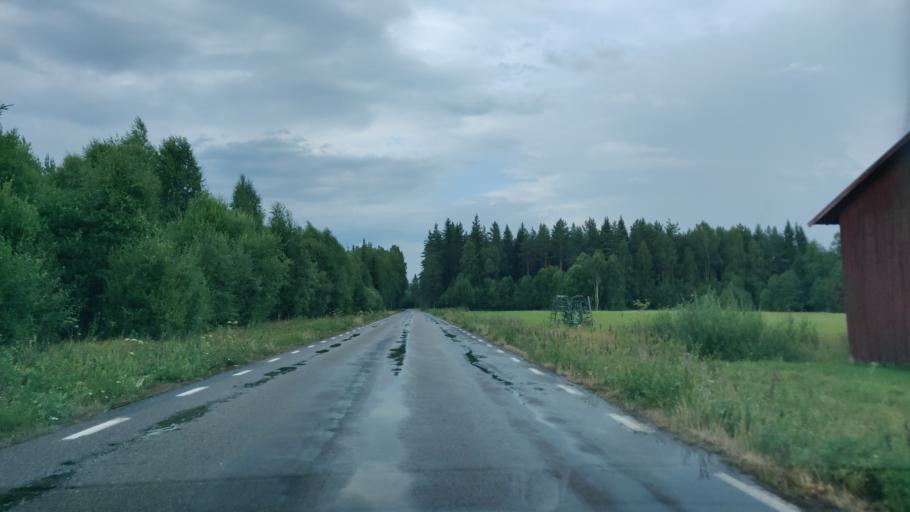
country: SE
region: Vaermland
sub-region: Munkfors Kommun
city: Munkfors
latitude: 59.8815
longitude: 13.5216
